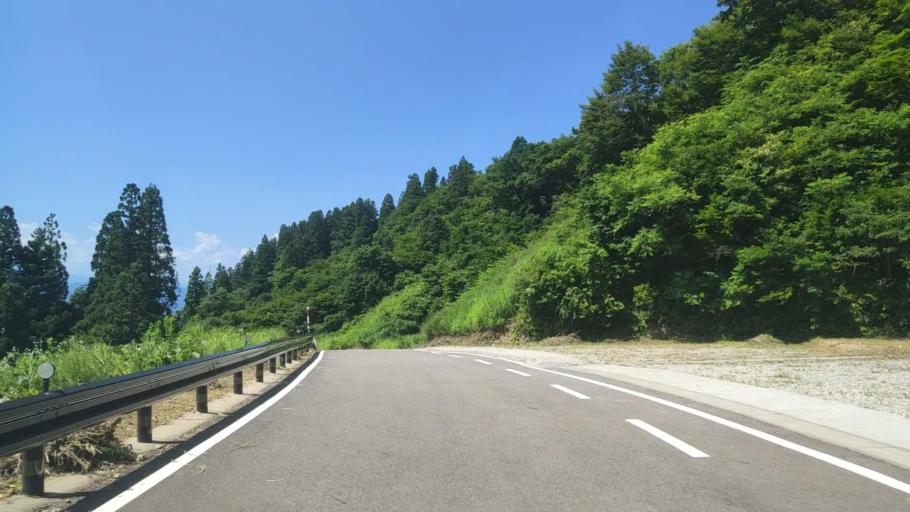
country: JP
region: Fukui
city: Katsuyama
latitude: 36.1419
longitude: 136.5194
